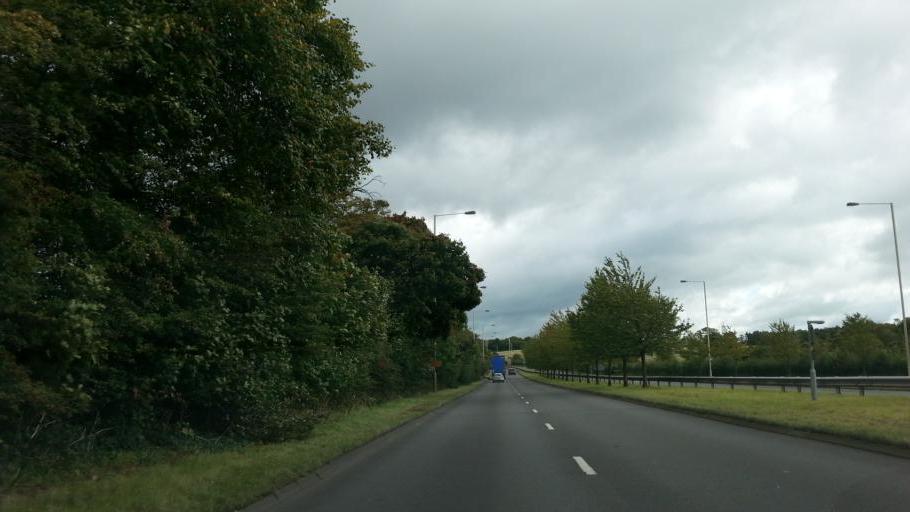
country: GB
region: England
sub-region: Dudley
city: Halesowen
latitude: 52.4475
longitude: -2.0276
